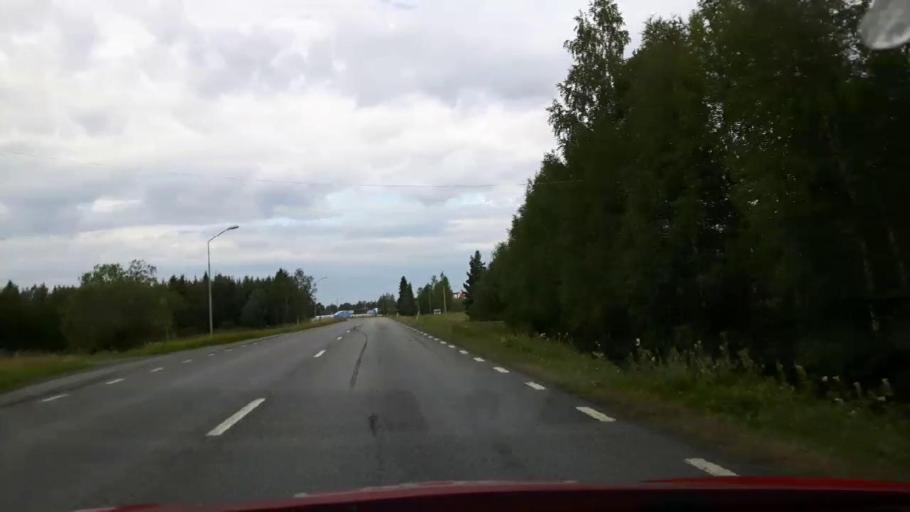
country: SE
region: Jaemtland
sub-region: Stroemsunds Kommun
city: Stroemsund
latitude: 63.5679
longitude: 15.3641
